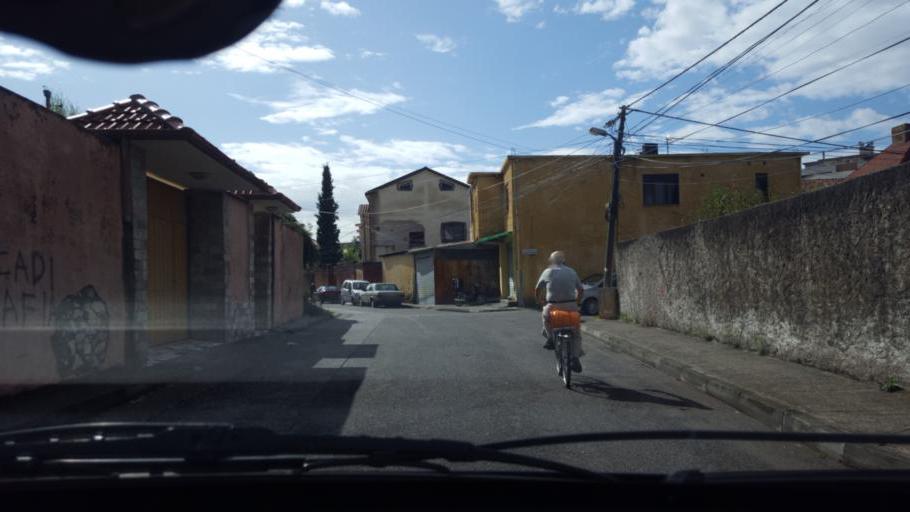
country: AL
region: Shkoder
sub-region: Rrethi i Shkodres
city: Shkoder
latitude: 42.0729
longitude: 19.5078
